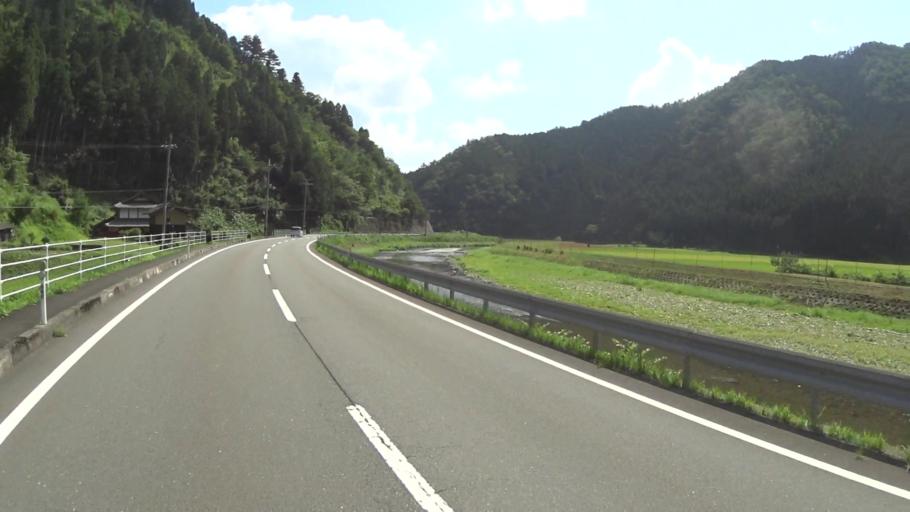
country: JP
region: Fukui
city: Obama
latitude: 35.3290
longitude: 135.5668
